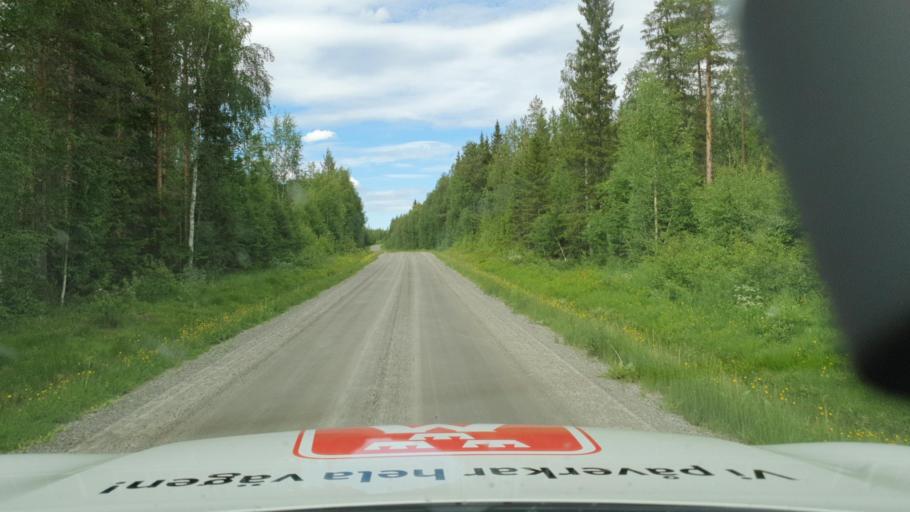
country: SE
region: Vaesterbotten
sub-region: Norsjo Kommun
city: Norsjoe
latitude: 64.8305
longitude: 19.7012
